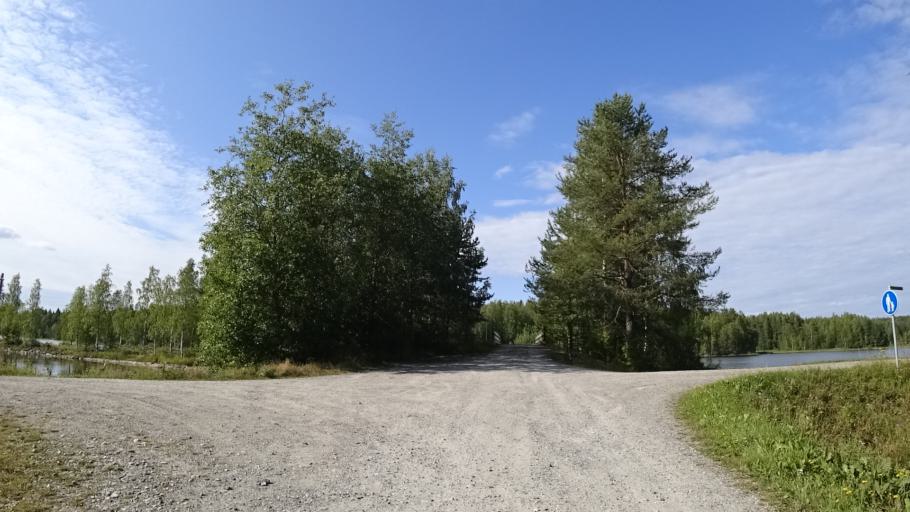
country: FI
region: North Karelia
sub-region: Joensuu
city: Eno
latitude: 62.8009
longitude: 30.1486
